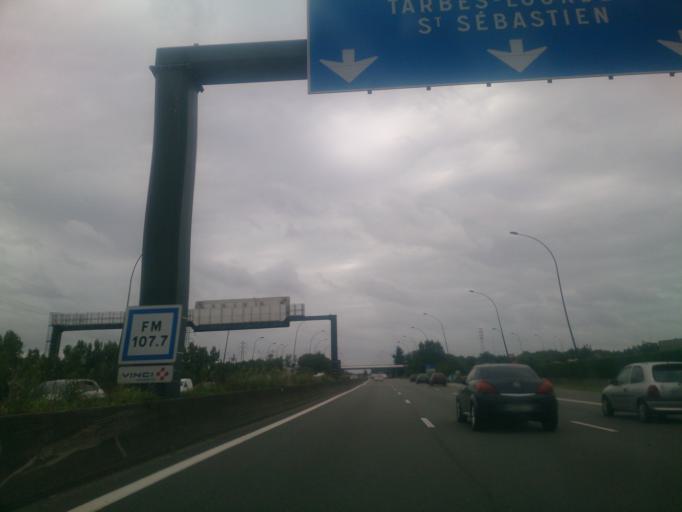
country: FR
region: Midi-Pyrenees
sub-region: Departement de la Haute-Garonne
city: Portet-sur-Garonne
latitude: 43.5573
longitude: 1.4124
